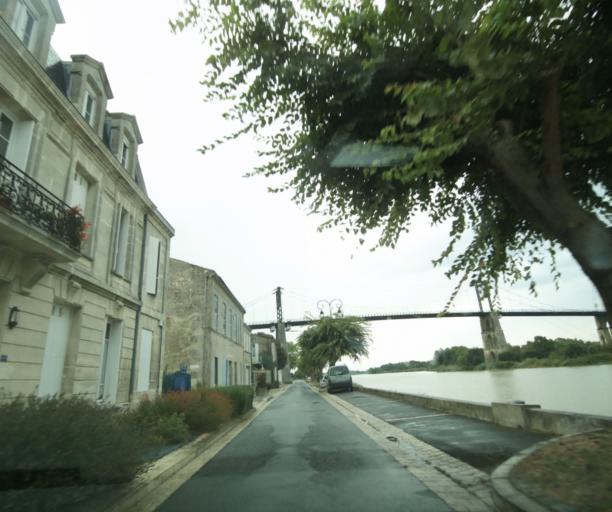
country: FR
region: Poitou-Charentes
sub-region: Departement de la Charente-Maritime
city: Tonnay-Charente
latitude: 45.9412
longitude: -0.8873
